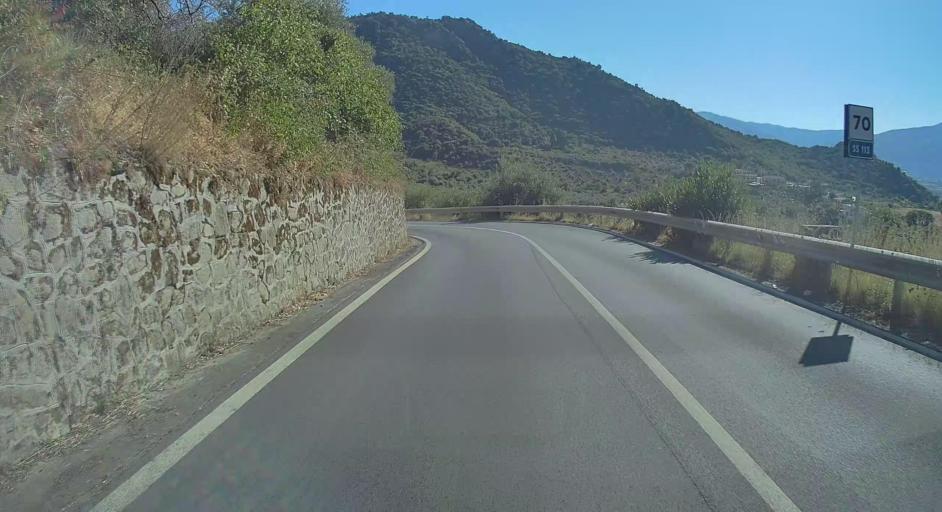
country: IT
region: Sicily
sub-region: Messina
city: Oliveri
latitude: 38.1414
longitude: 15.0240
